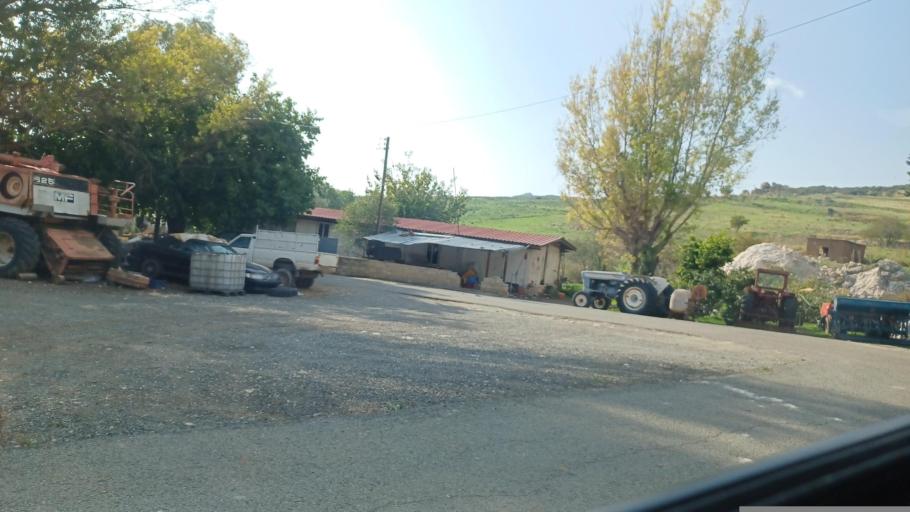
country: CY
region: Limassol
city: Pissouri
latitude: 34.7620
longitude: 32.6251
